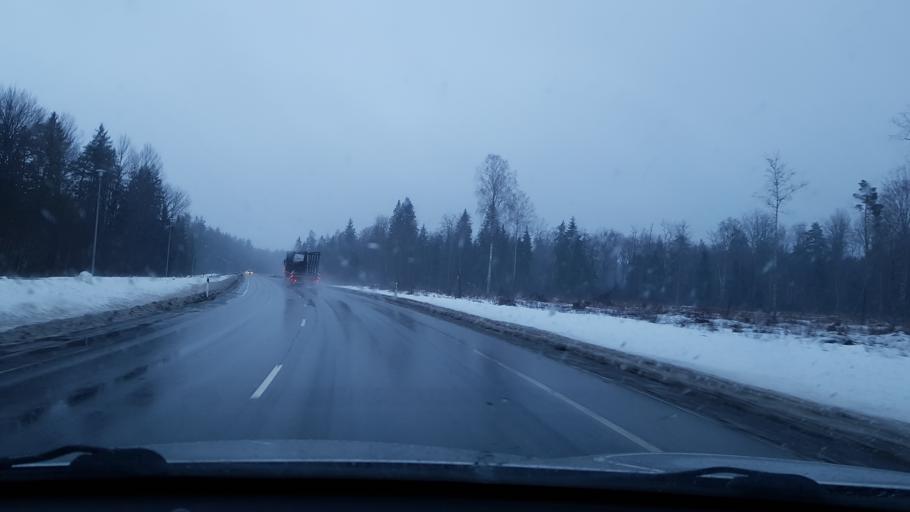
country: EE
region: Jaervamaa
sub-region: Tueri vald
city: Tueri
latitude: 58.8566
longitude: 25.4858
